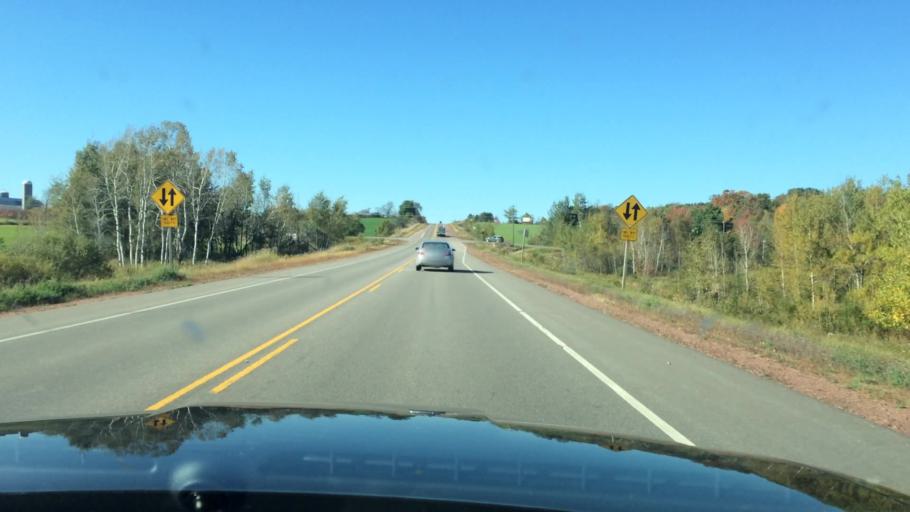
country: US
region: Wisconsin
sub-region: Marathon County
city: Wausau
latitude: 45.0009
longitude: -89.6676
